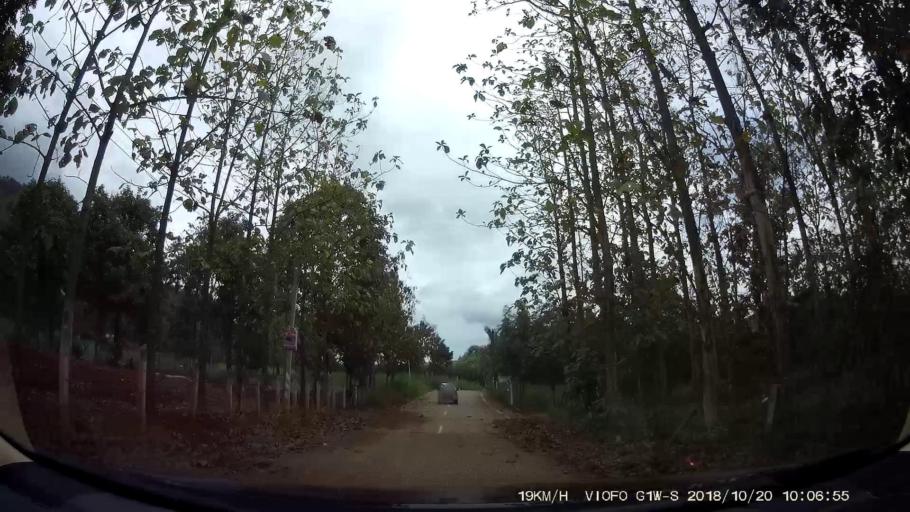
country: TH
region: Chaiyaphum
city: Khon San
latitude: 16.5462
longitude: 101.8522
